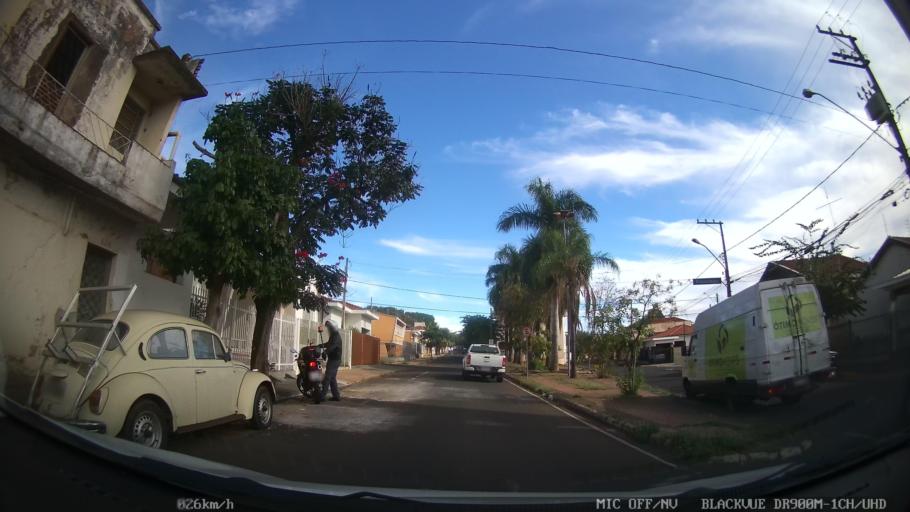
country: BR
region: Sao Paulo
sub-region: Catanduva
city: Catanduva
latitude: -21.1326
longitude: -48.9792
